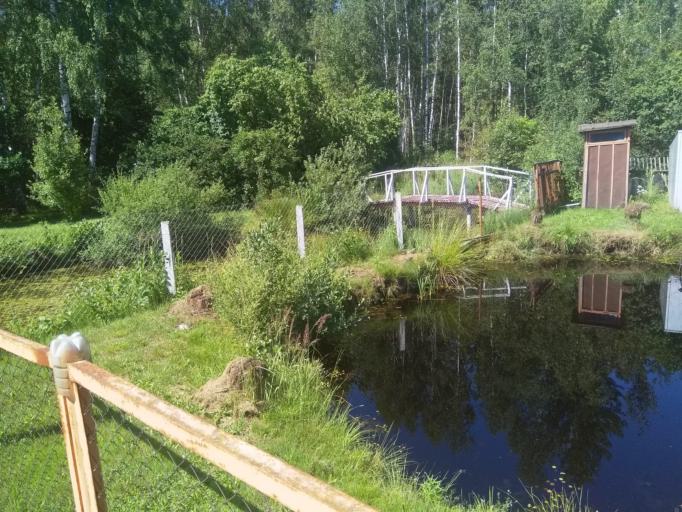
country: BY
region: Mogilev
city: Dashkawka
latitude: 53.6869
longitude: 30.2616
